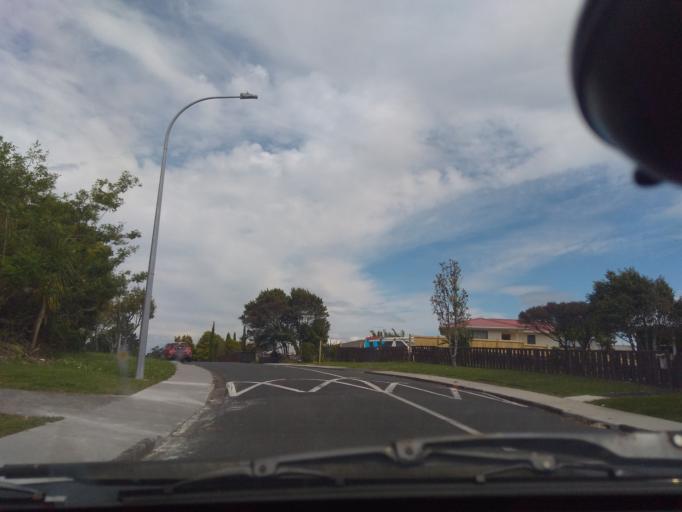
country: NZ
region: Auckland
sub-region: Auckland
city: Waitakere
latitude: -36.9283
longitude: 174.6720
